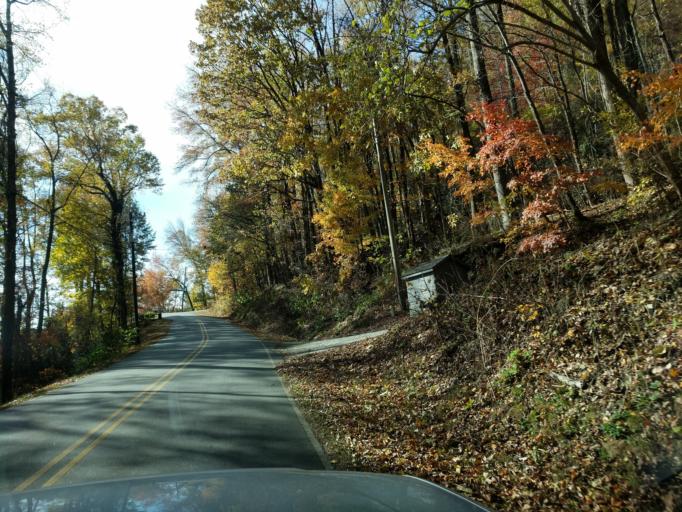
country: US
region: North Carolina
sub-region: Polk County
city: Columbus
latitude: 35.2710
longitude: -82.2108
